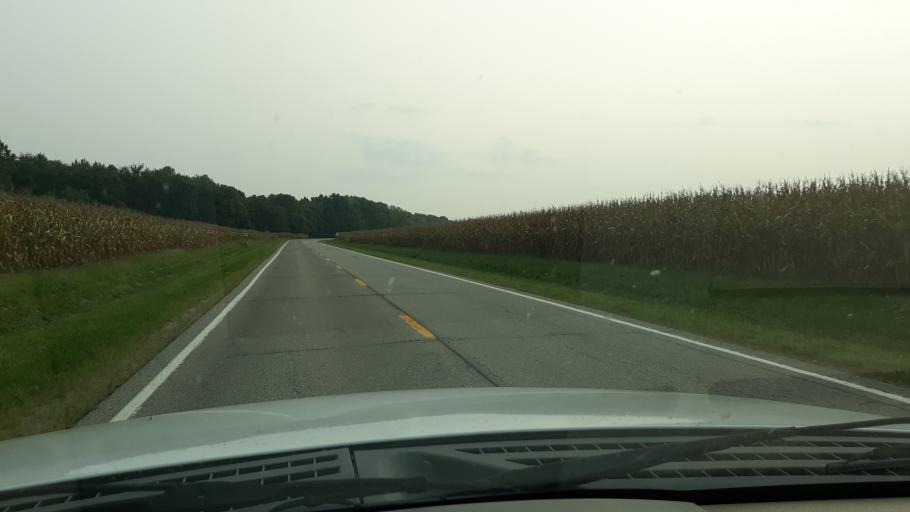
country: US
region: Illinois
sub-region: Edwards County
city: Grayville
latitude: 38.3092
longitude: -87.9417
